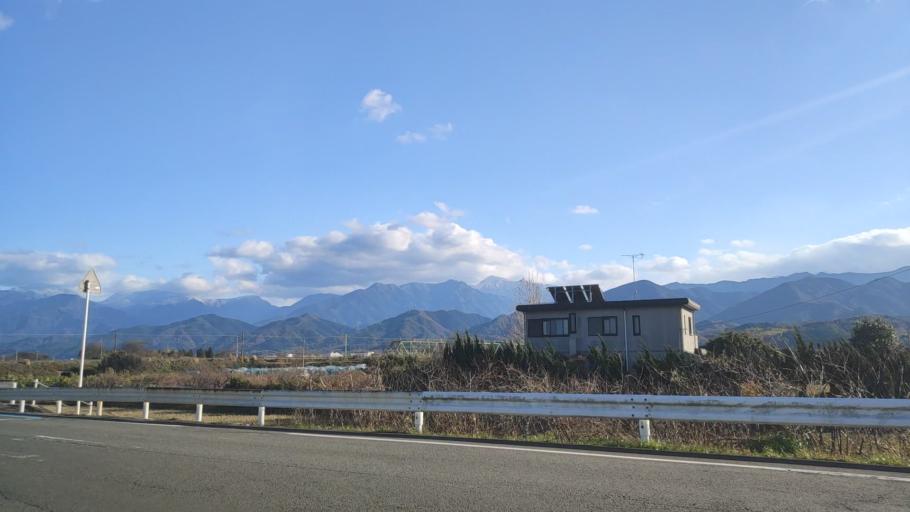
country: JP
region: Ehime
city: Saijo
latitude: 33.9084
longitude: 133.0969
